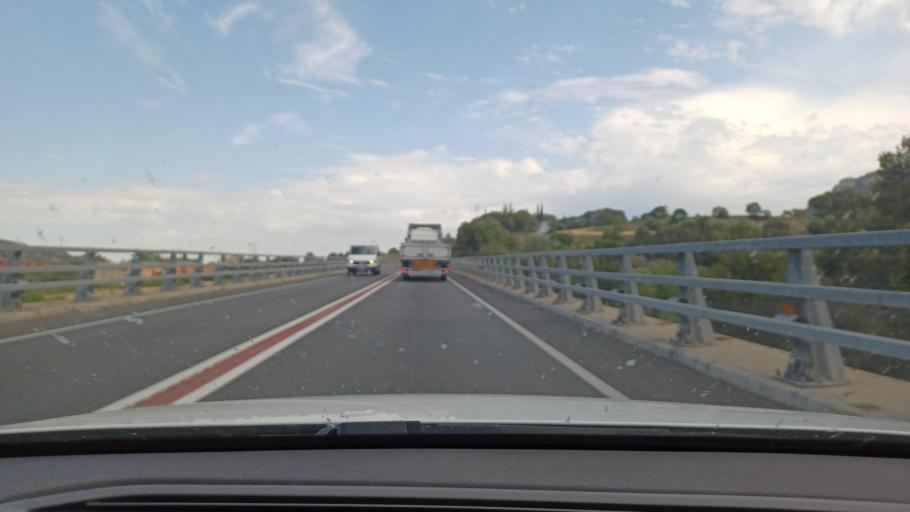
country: ES
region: Catalonia
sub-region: Provincia de Barcelona
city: La Pobla de Claramunt
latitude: 41.5547
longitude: 1.6866
